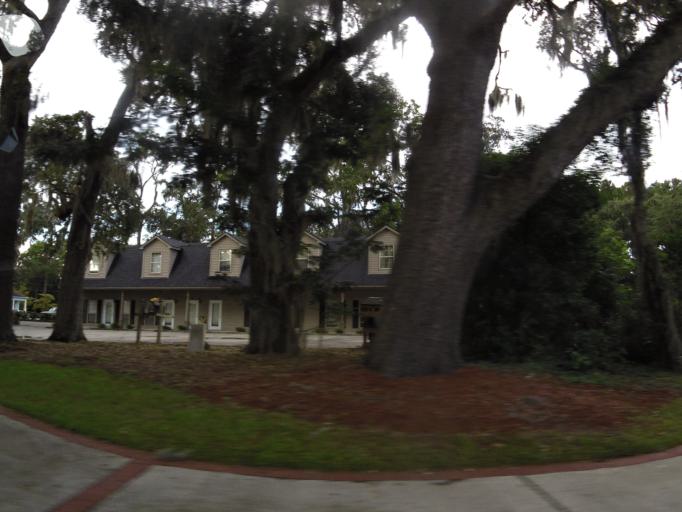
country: US
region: Georgia
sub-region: Liberty County
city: Hinesville
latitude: 31.8499
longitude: -81.5949
